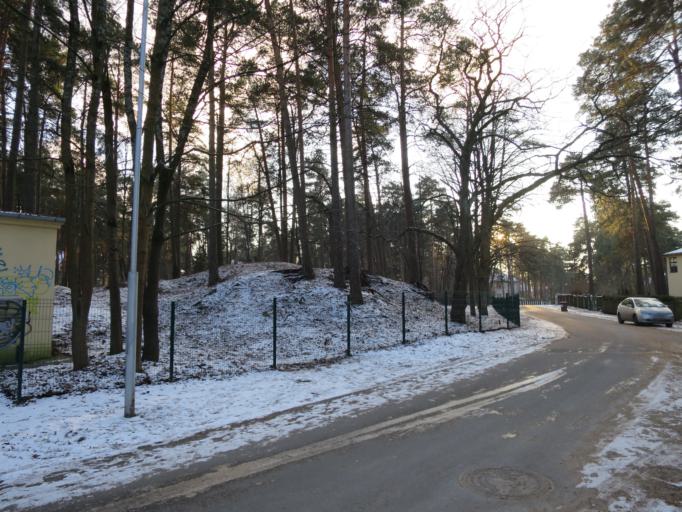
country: LV
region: Riga
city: Jaunciems
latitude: 57.0015
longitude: 24.1657
